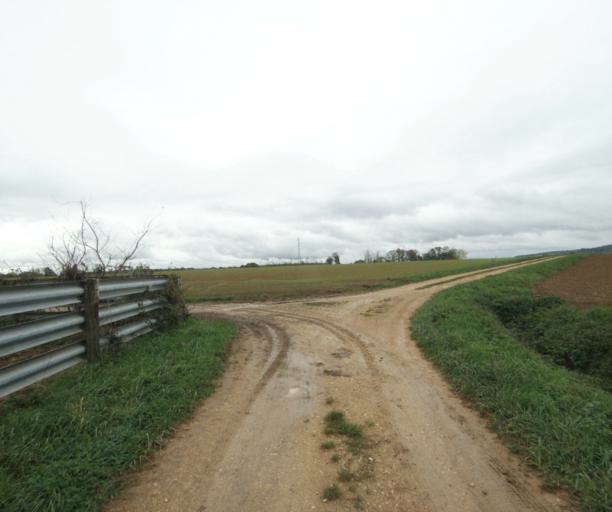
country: FR
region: Rhone-Alpes
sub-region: Departement de l'Ain
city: Pont-de-Vaux
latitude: 46.4625
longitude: 4.8670
